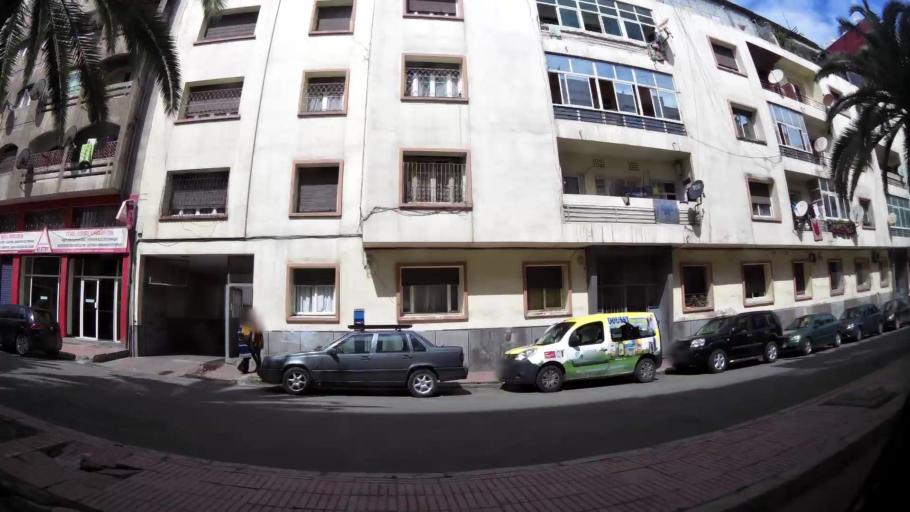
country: MA
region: Grand Casablanca
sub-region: Casablanca
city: Casablanca
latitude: 33.5950
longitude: -7.5935
